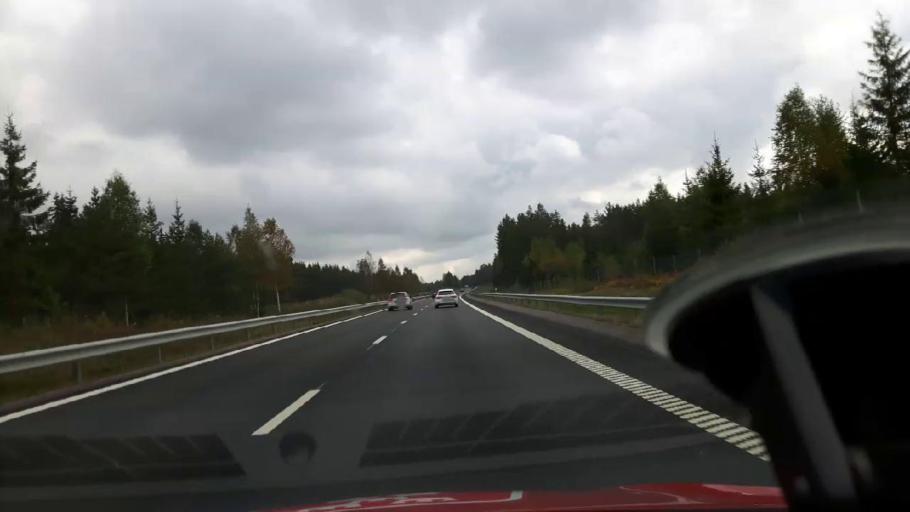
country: SE
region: Gaevleborg
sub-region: Gavle Kommun
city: Gavle
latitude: 60.6020
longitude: 17.1821
